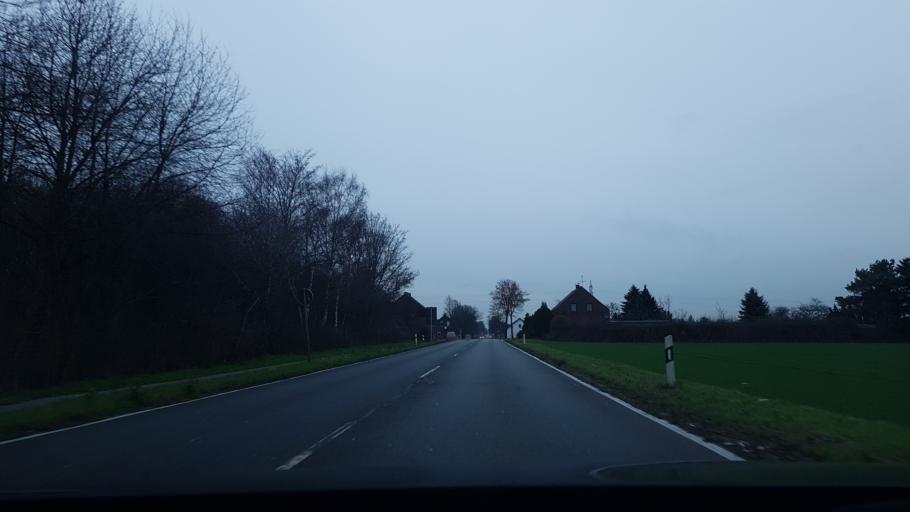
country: DE
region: North Rhine-Westphalia
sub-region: Regierungsbezirk Dusseldorf
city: Moers
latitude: 51.4147
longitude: 6.6592
